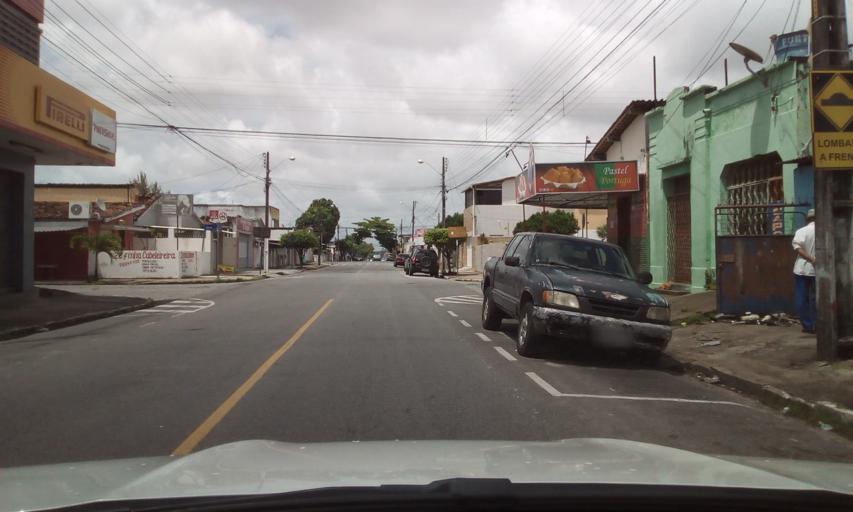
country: BR
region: Paraiba
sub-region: Joao Pessoa
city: Joao Pessoa
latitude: -7.1313
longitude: -34.8775
